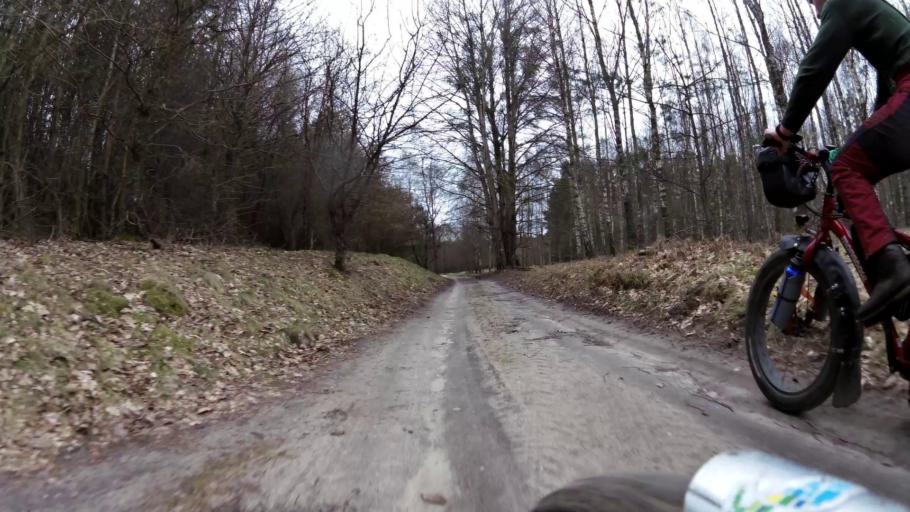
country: PL
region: Pomeranian Voivodeship
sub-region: Powiat bytowski
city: Trzebielino
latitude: 54.1179
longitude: 17.1285
